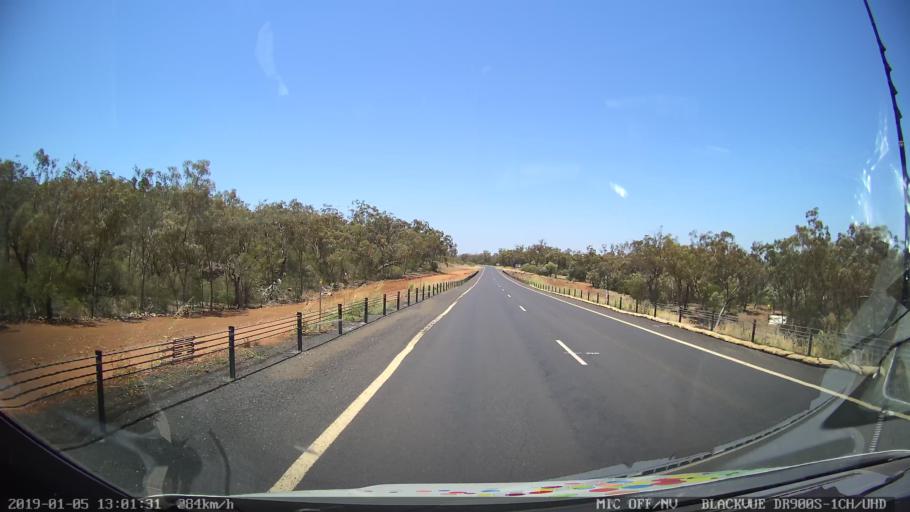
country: AU
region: New South Wales
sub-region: Narrabri
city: Boggabri
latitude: -31.1151
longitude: 149.7982
